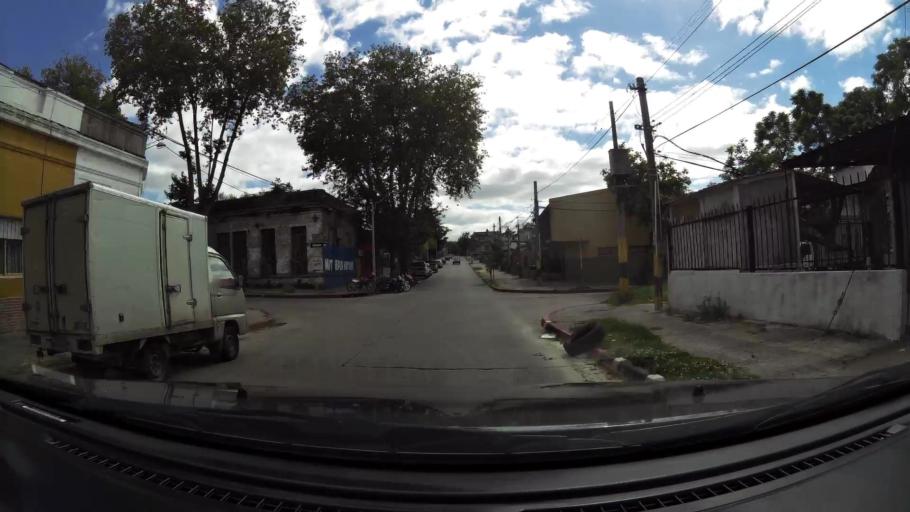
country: UY
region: Montevideo
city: Montevideo
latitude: -34.8797
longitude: -56.1447
